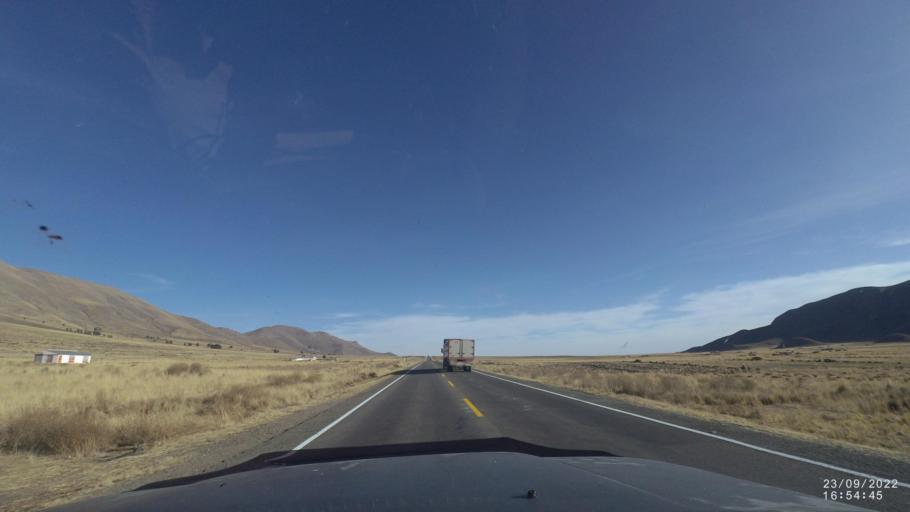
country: BO
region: Oruro
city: Poopo
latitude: -18.4689
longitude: -66.9682
